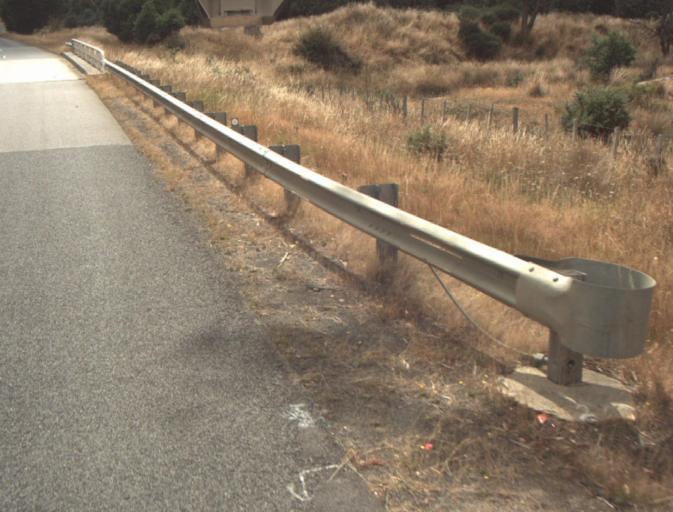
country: AU
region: Tasmania
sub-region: Northern Midlands
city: Evandale
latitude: -41.4775
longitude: 147.5156
